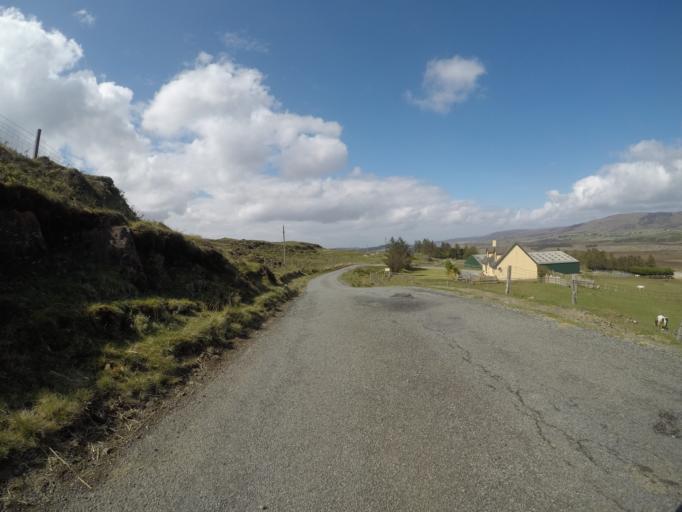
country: GB
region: Scotland
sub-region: Highland
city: Isle of Skye
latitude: 57.4244
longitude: -6.2681
